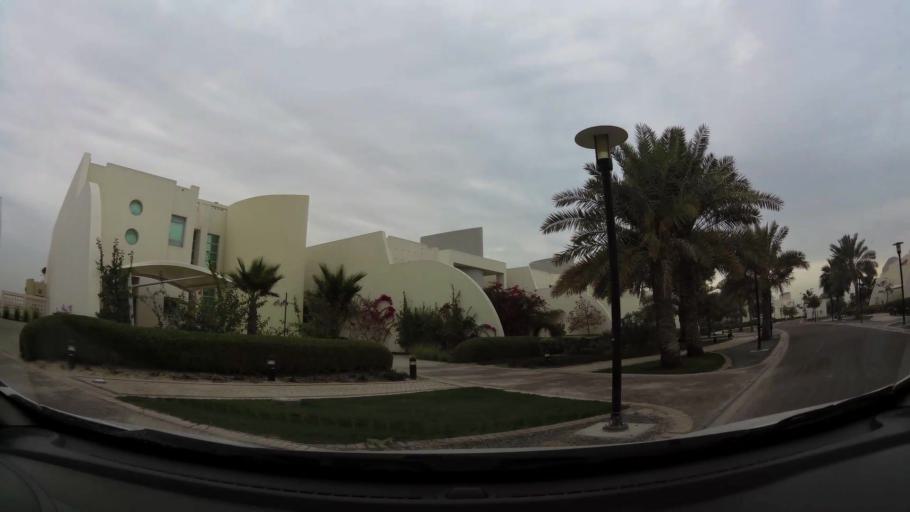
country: BH
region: Central Governorate
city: Dar Kulayb
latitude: 25.8289
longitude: 50.6153
